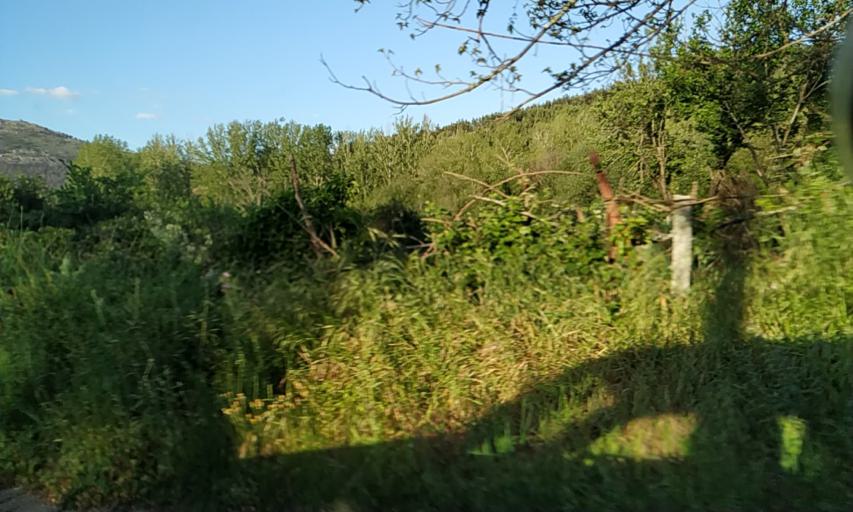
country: PT
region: Portalegre
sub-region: Marvao
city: Marvao
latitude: 39.3793
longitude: -7.3883
